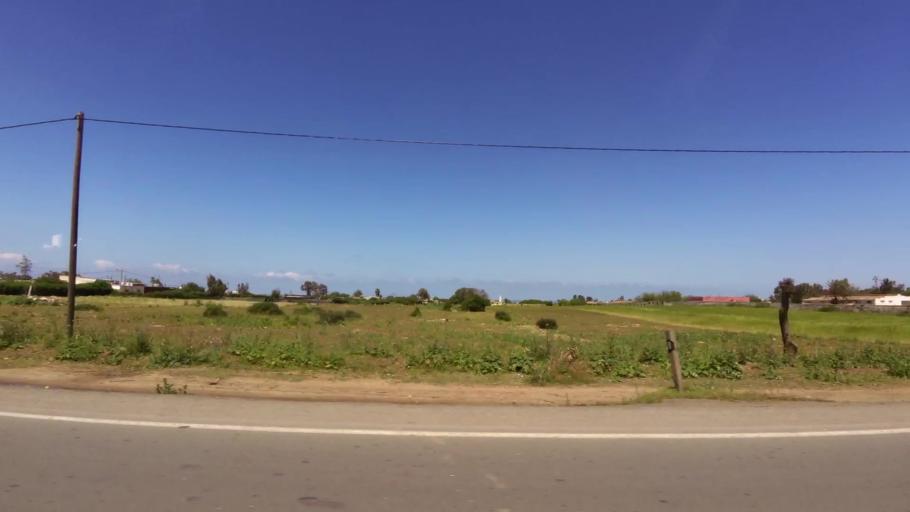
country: MA
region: Grand Casablanca
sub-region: Nouaceur
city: Dar Bouazza
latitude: 33.5171
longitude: -7.8039
